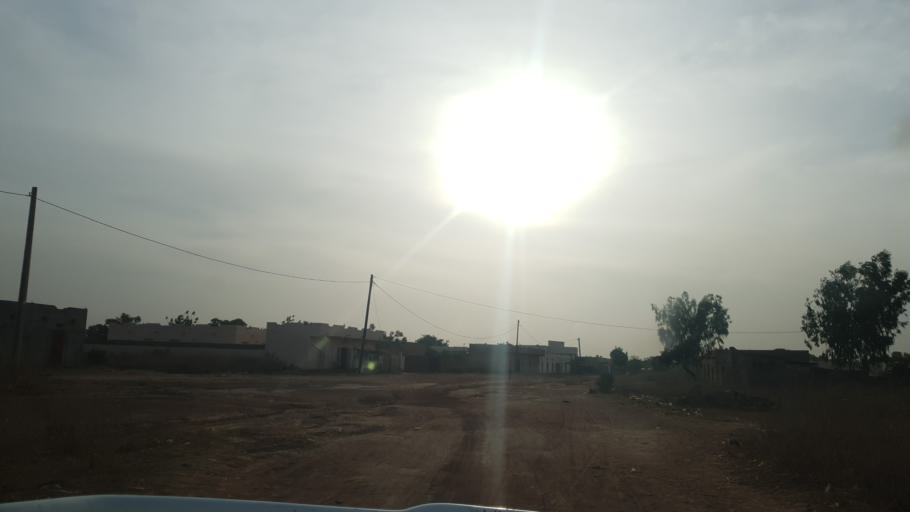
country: ML
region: Segou
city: Baroueli
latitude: 12.7741
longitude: -6.9375
